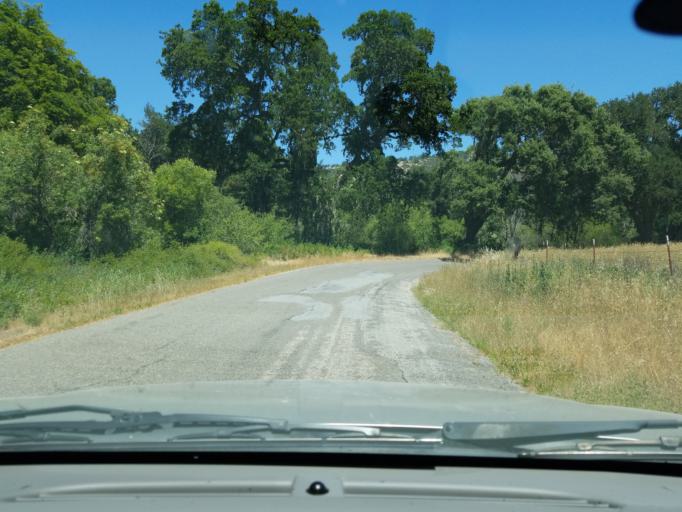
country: US
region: California
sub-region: Monterey County
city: Gonzales
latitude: 36.3510
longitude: -121.5433
